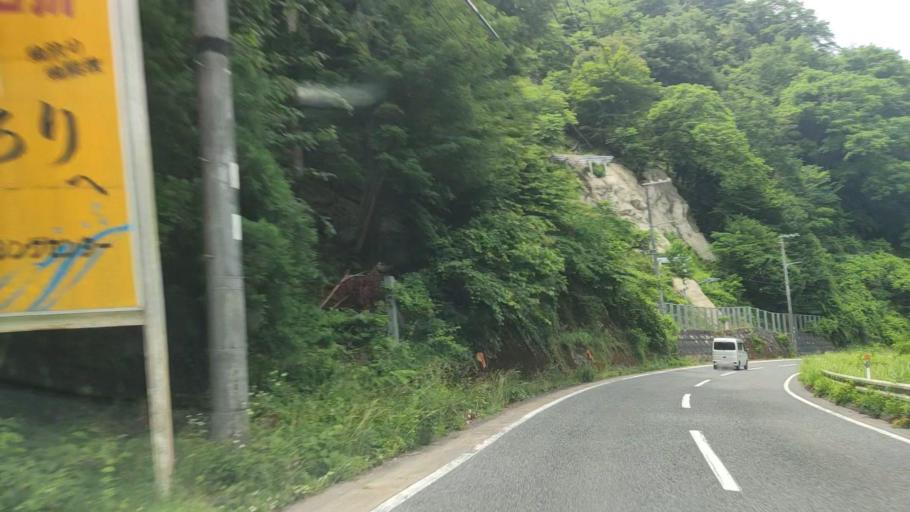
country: JP
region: Hyogo
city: Toyooka
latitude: 35.4798
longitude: 134.6124
